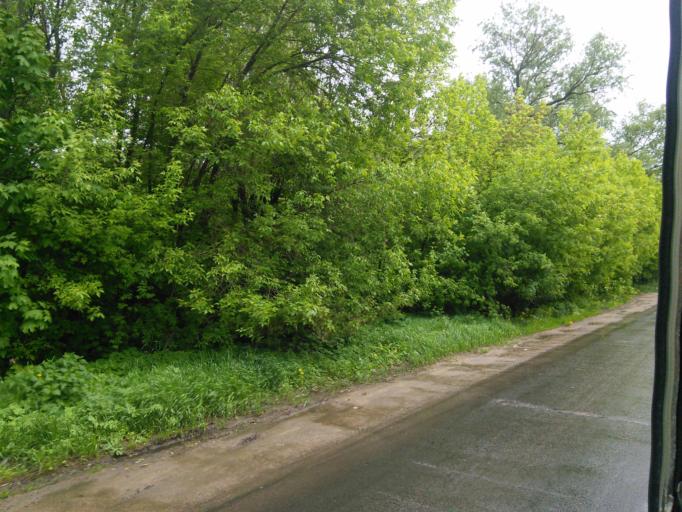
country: RU
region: Moskovskaya
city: Serpukhov
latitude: 54.9301
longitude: 37.3683
